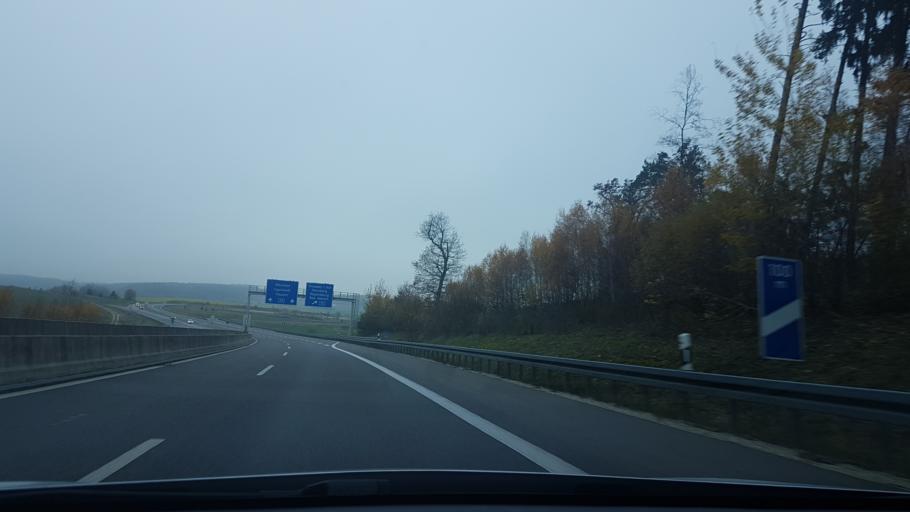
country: DE
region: Bavaria
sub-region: Lower Bavaria
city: Bad Abbach
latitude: 48.8875
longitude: 12.0825
